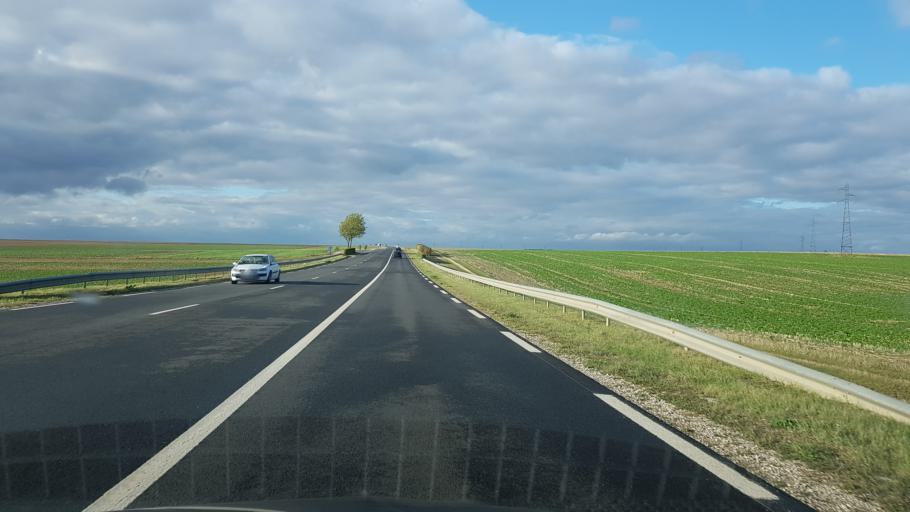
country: FR
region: Centre
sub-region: Departement du Loiret
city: Sermaises
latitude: 48.3285
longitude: 2.1961
